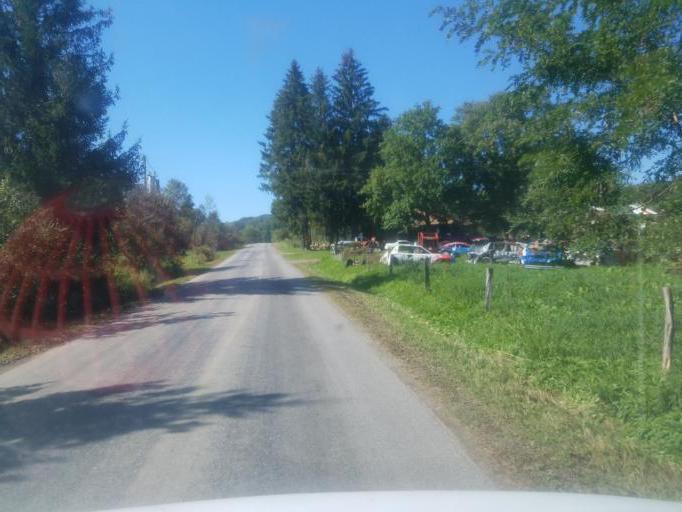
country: US
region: New York
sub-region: Allegany County
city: Friendship
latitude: 42.3010
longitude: -78.1936
